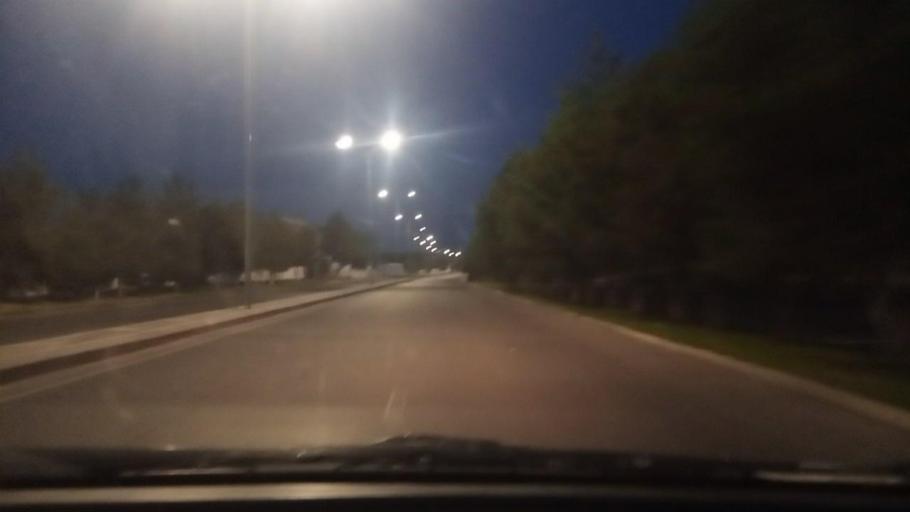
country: UZ
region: Toshkent Shahri
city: Tashkent
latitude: 41.2498
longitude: 69.2112
